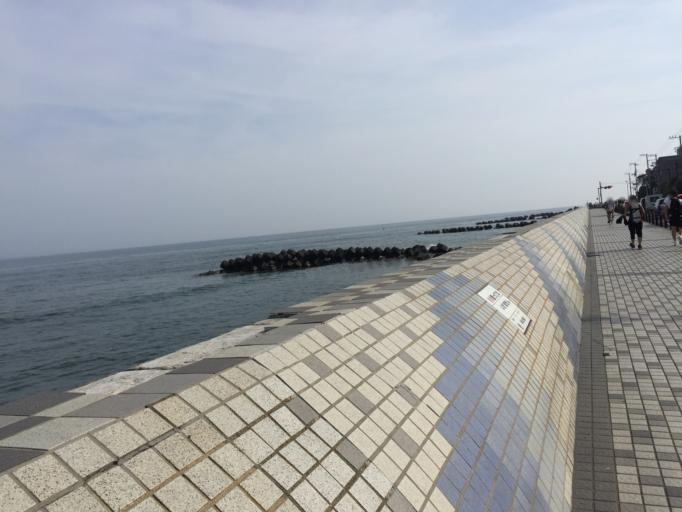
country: JP
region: Kanagawa
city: Kamakura
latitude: 35.3069
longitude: 139.5334
